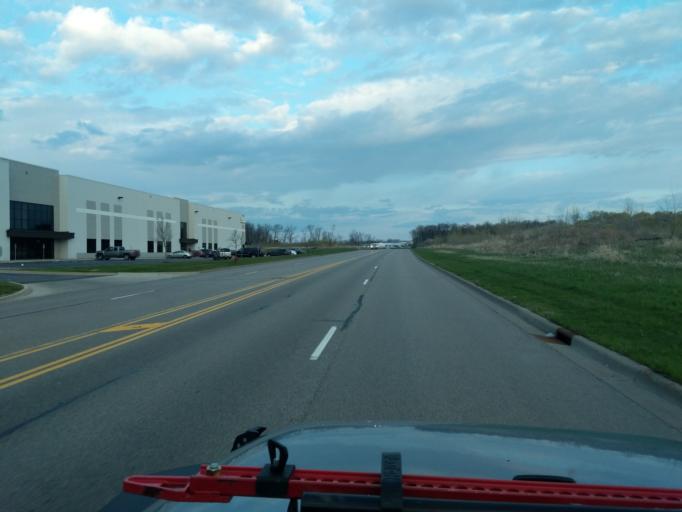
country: US
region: Minnesota
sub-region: Hennepin County
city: Rogers
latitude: 45.1830
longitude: -93.5253
